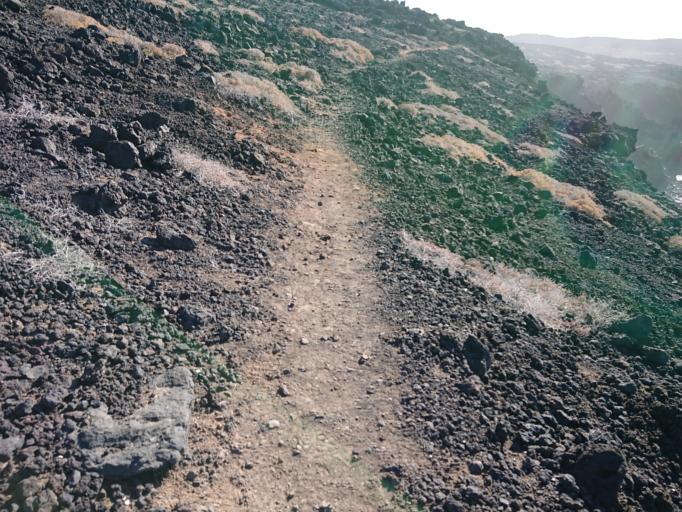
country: ES
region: Canary Islands
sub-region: Provincia de Las Palmas
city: Tinajo
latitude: 29.0821
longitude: -13.7262
